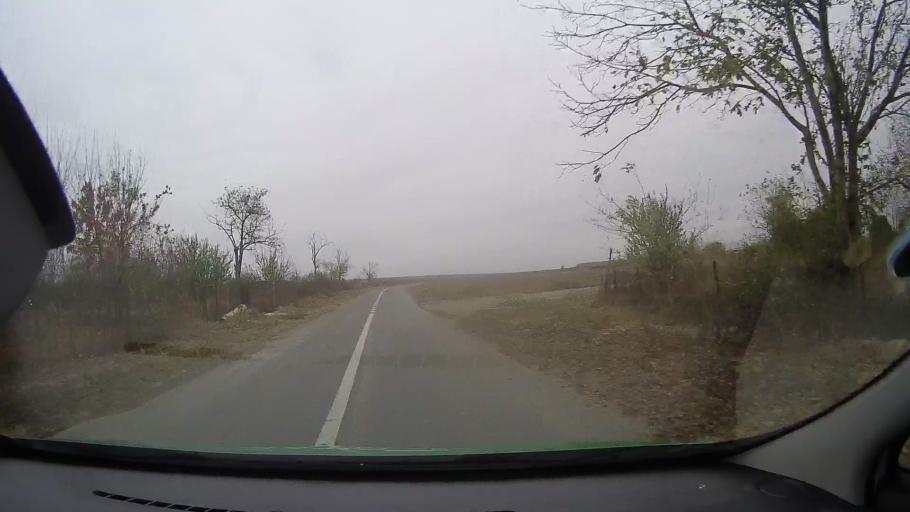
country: RO
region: Constanta
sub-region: Comuna Vulturu
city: Vulturu
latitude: 44.6564
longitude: 28.2667
